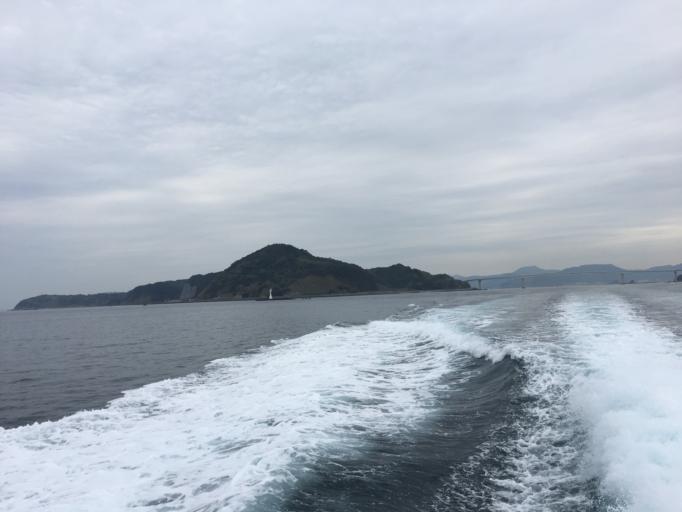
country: JP
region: Nagasaki
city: Nagasaki-shi
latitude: 32.6784
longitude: 129.7809
